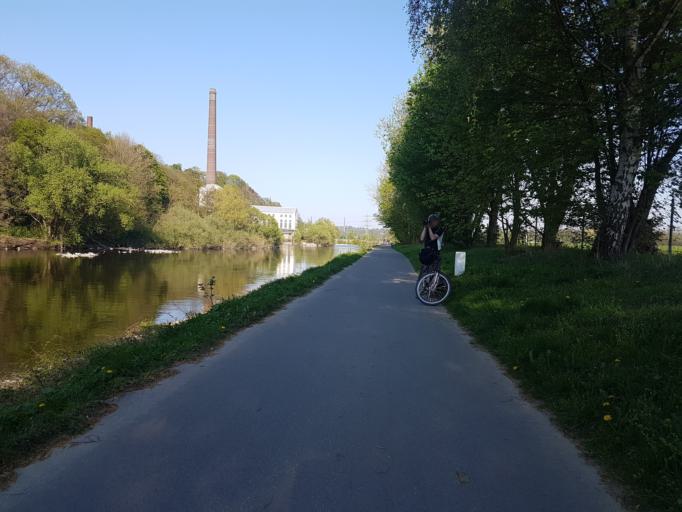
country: DE
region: North Rhine-Westphalia
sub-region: Regierungsbezirk Munster
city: Gelsenkirchen
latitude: 51.4284
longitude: 7.1052
